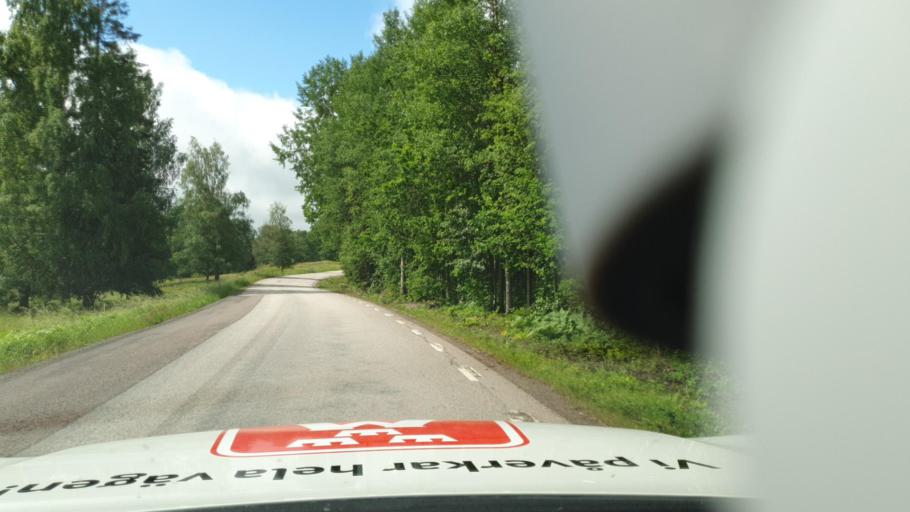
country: SE
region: Vaermland
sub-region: Kristinehamns Kommun
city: Bjorneborg
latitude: 59.0972
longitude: 14.2891
